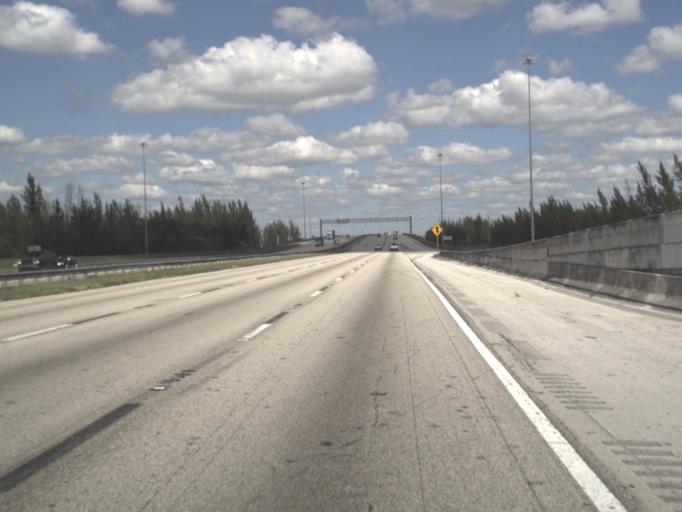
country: US
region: Florida
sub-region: Miami-Dade County
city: Doral
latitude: 25.8706
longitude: -80.3878
